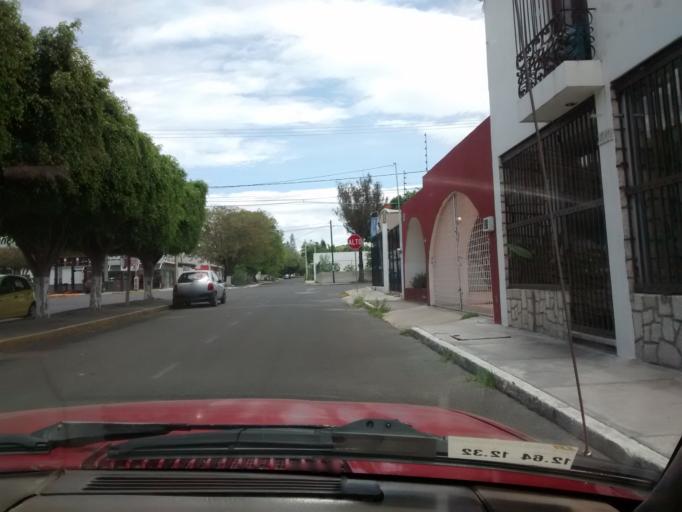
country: MX
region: Puebla
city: Tehuacan
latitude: 18.4614
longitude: -97.4091
